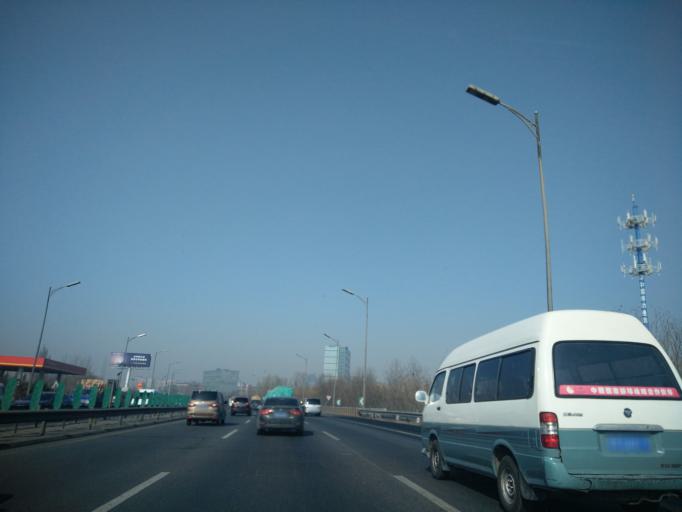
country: CN
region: Beijing
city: Wangjing
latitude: 40.0125
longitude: 116.4781
